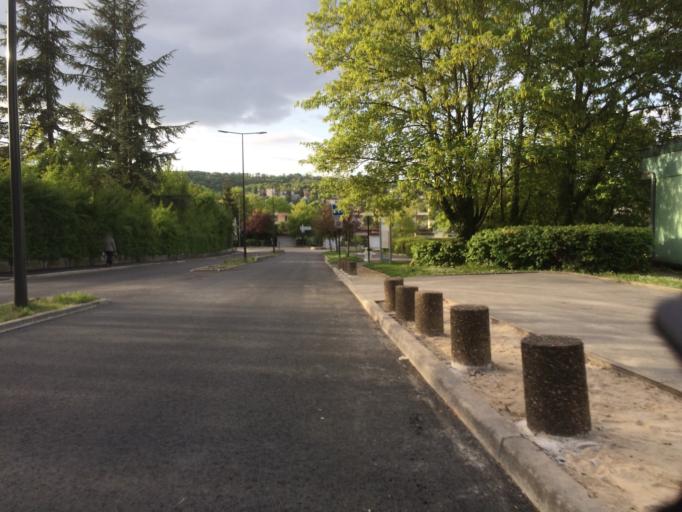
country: FR
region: Ile-de-France
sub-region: Departement de l'Essonne
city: Verrieres-le-Buisson
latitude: 48.7337
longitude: 2.2556
